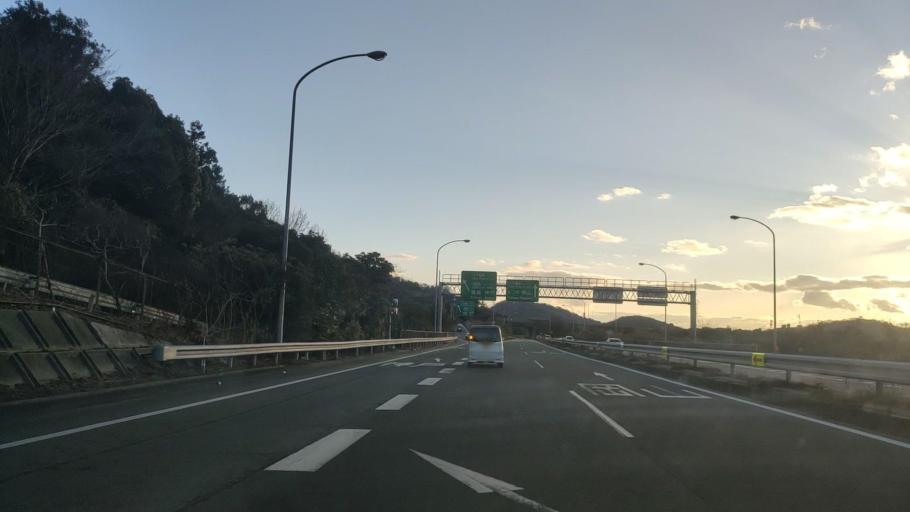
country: JP
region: Hyogo
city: Tatsunocho-tominaga
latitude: 34.8497
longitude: 134.6042
